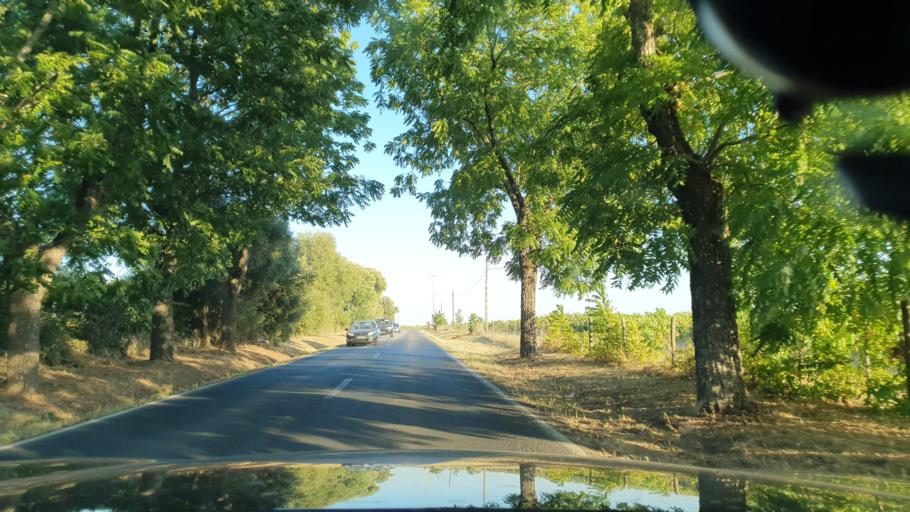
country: PT
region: Evora
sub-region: Estremoz
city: Estremoz
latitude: 38.8946
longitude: -7.6645
